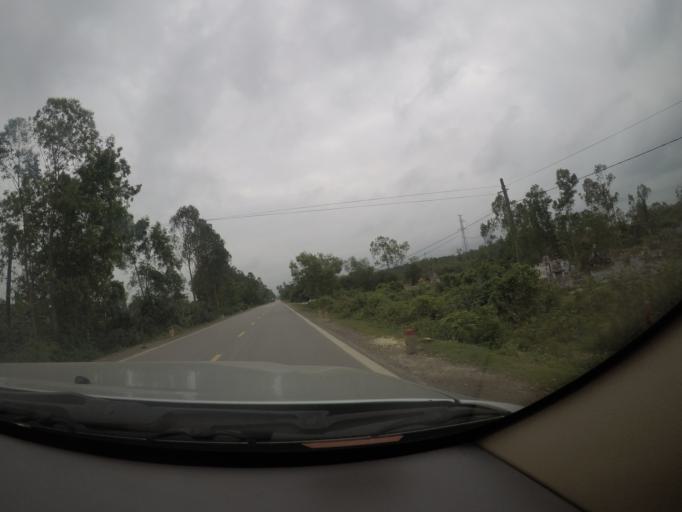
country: VN
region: Quang Binh
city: Quan Hau
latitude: 17.2988
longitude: 106.6420
